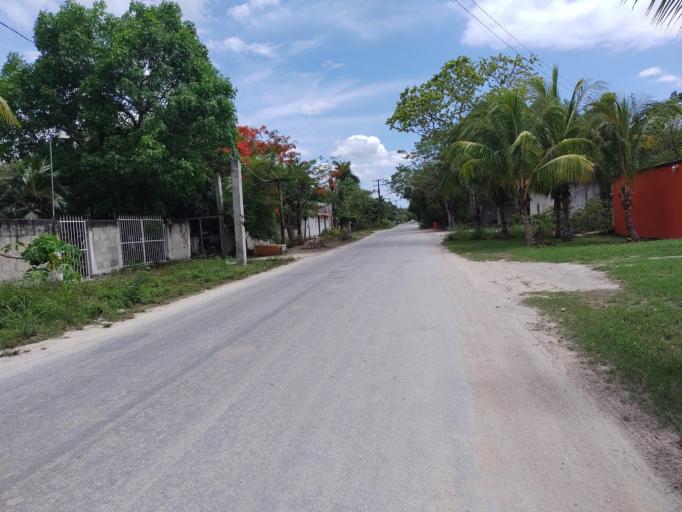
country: MX
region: Quintana Roo
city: San Miguel de Cozumel
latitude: 20.4848
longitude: -86.9116
